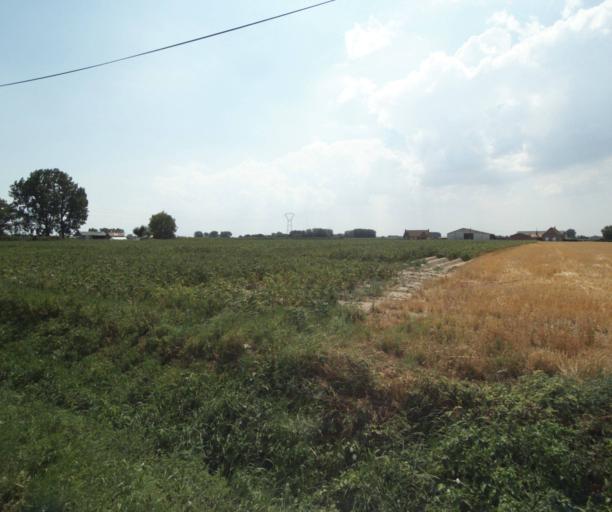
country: FR
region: Nord-Pas-de-Calais
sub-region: Departement du Nord
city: Comines
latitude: 50.7429
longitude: 2.9932
